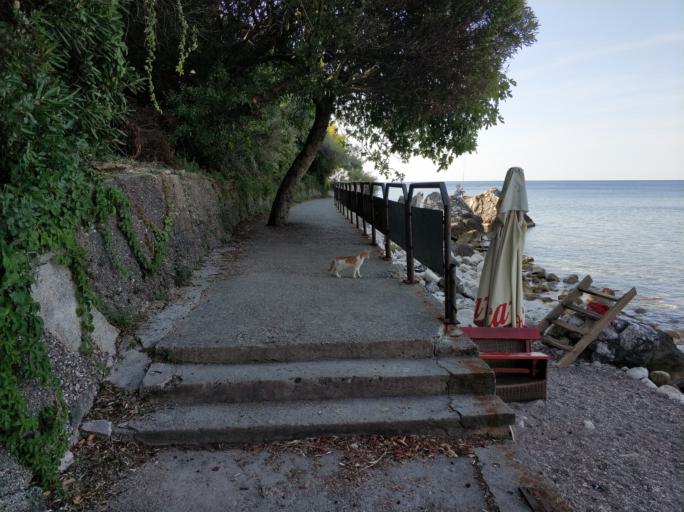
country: ME
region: Budva
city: Budva
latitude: 42.2739
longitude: 18.8883
